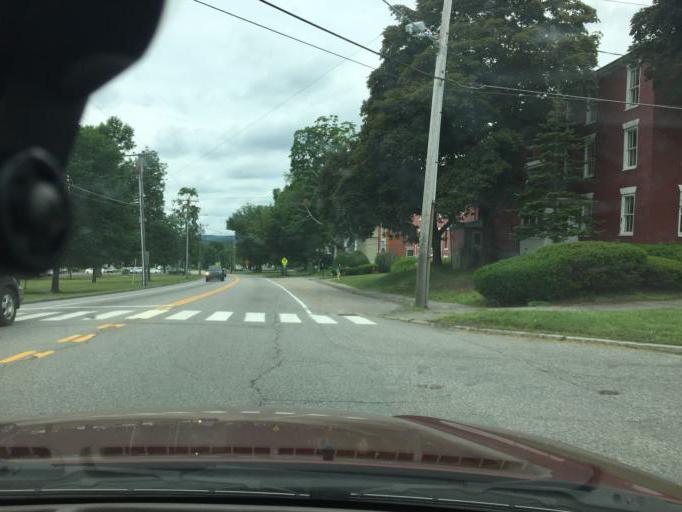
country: US
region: Connecticut
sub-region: Litchfield County
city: Litchfield
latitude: 41.7474
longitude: -73.1901
